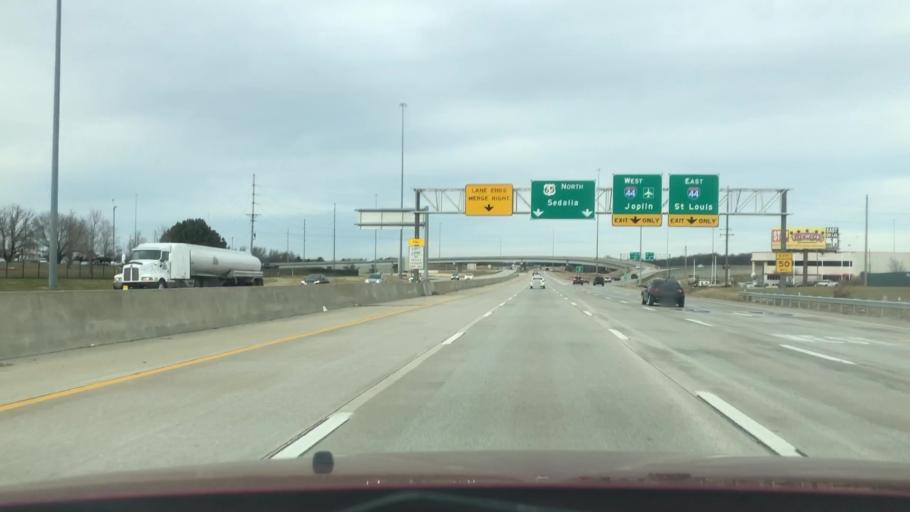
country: US
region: Missouri
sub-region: Greene County
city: Springfield
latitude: 37.2447
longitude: -93.2245
